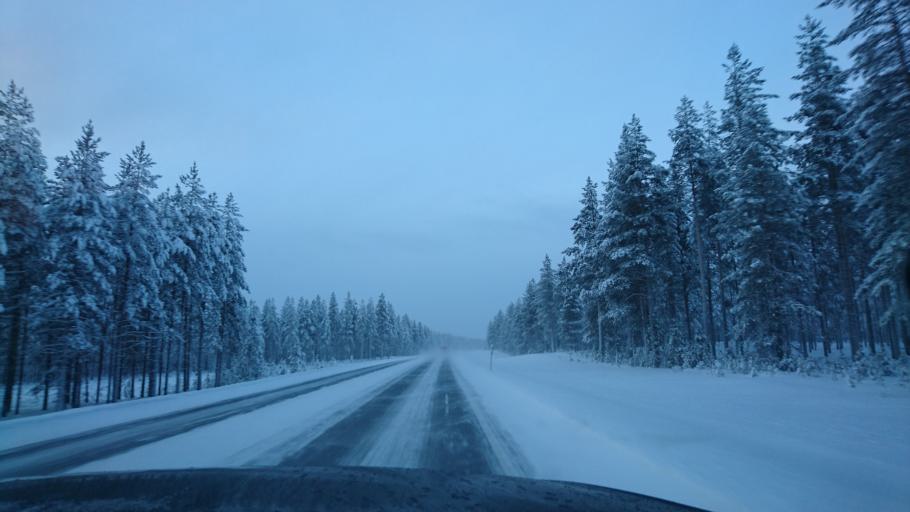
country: FI
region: Kainuu
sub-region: Kehys-Kainuu
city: Puolanka
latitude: 65.4317
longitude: 27.5694
